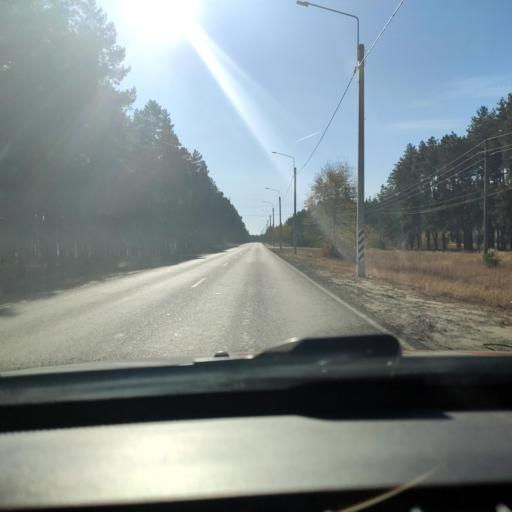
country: RU
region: Voronezj
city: Shilovo
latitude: 51.5352
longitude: 39.1394
